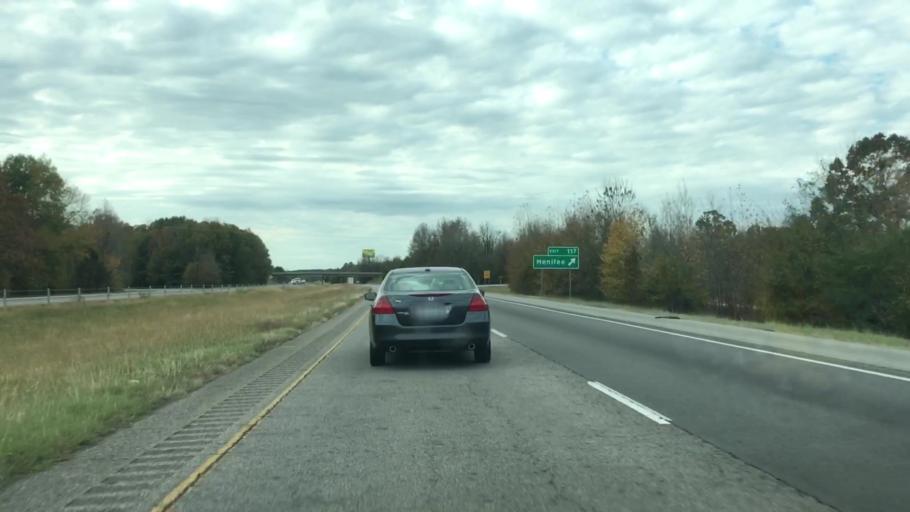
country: US
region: Arkansas
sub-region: Faulkner County
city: Conway
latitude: 35.1516
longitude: -92.5482
